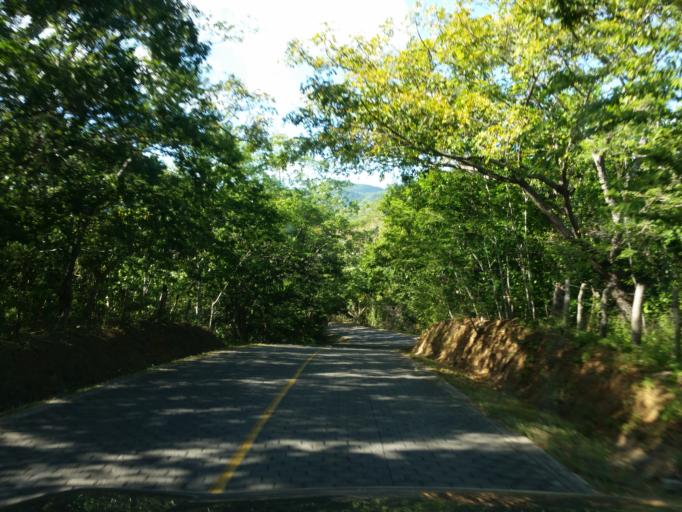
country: NI
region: Rivas
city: San Juan del Sur
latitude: 11.2406
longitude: -85.8339
